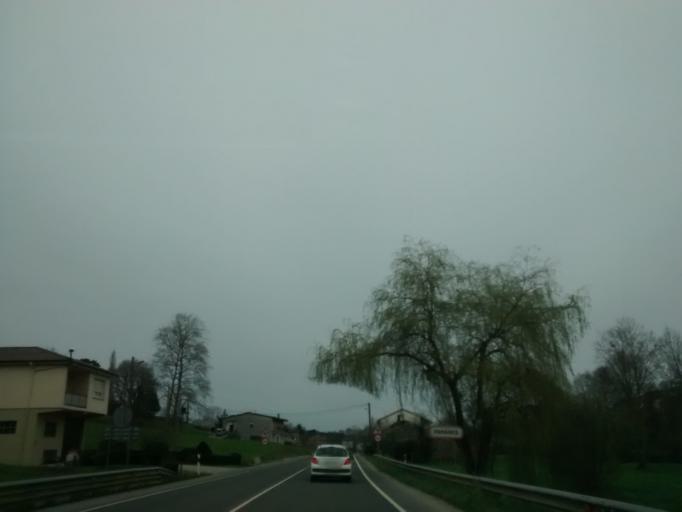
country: ES
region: Cantabria
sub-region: Provincia de Cantabria
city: Penagos
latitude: 43.3524
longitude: -3.7807
